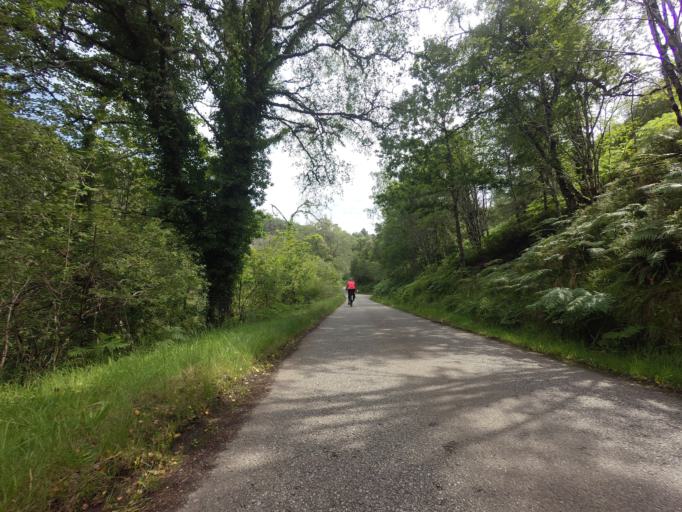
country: GB
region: Scotland
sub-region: Highland
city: Evanton
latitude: 57.9502
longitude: -4.4042
